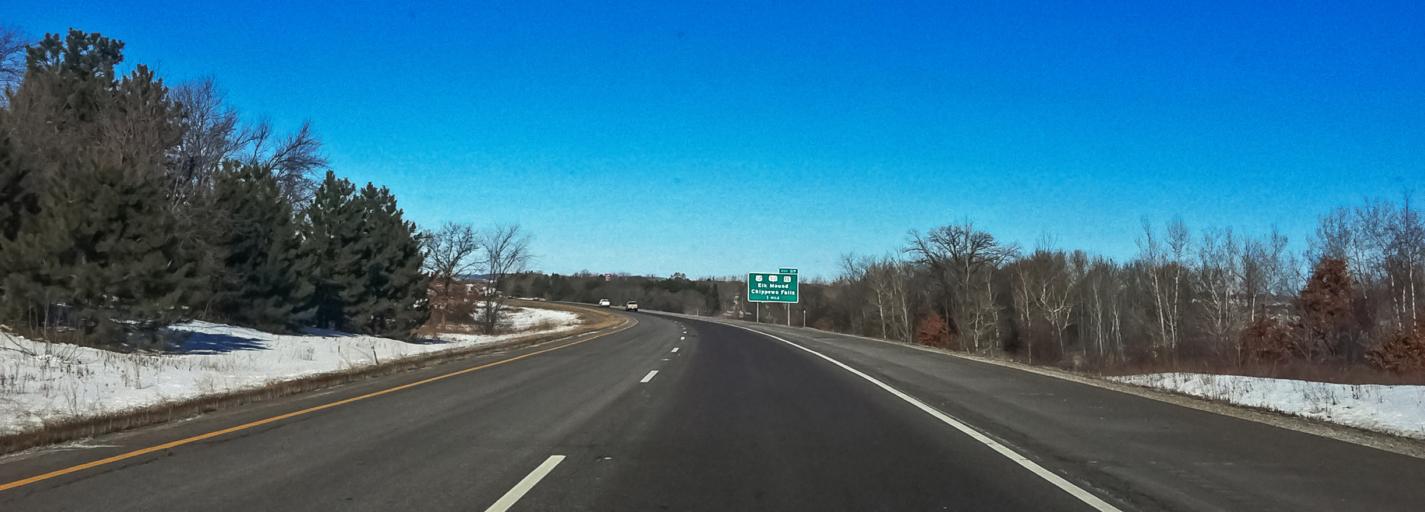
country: US
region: Wisconsin
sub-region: Eau Claire County
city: Eau Claire
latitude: 44.8315
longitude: -91.5788
